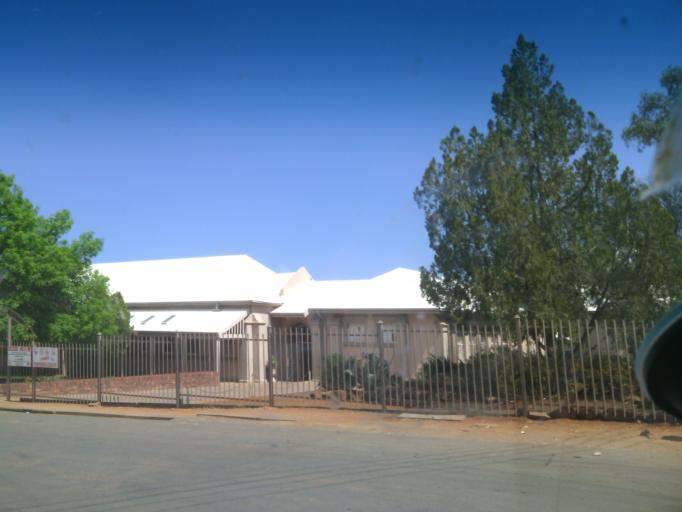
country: ZA
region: Northern Cape
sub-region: Frances Baard District Municipality
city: Barkly West
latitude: -28.5372
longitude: 24.5172
